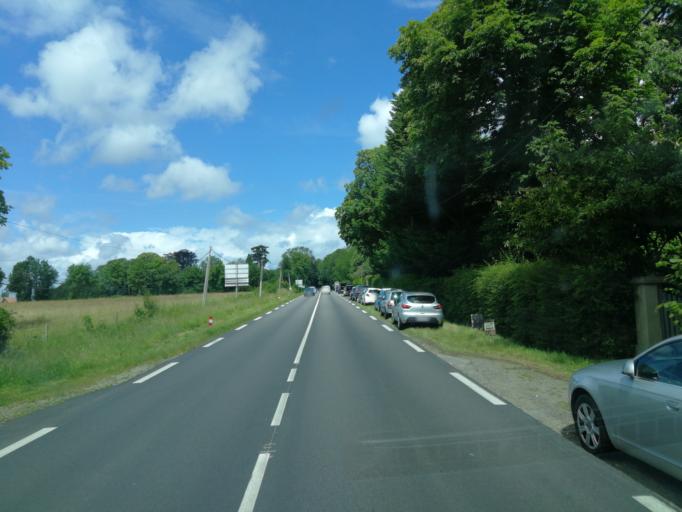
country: FR
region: Haute-Normandie
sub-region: Departement de la Seine-Maritime
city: Sahurs
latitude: 49.3465
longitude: 0.9302
